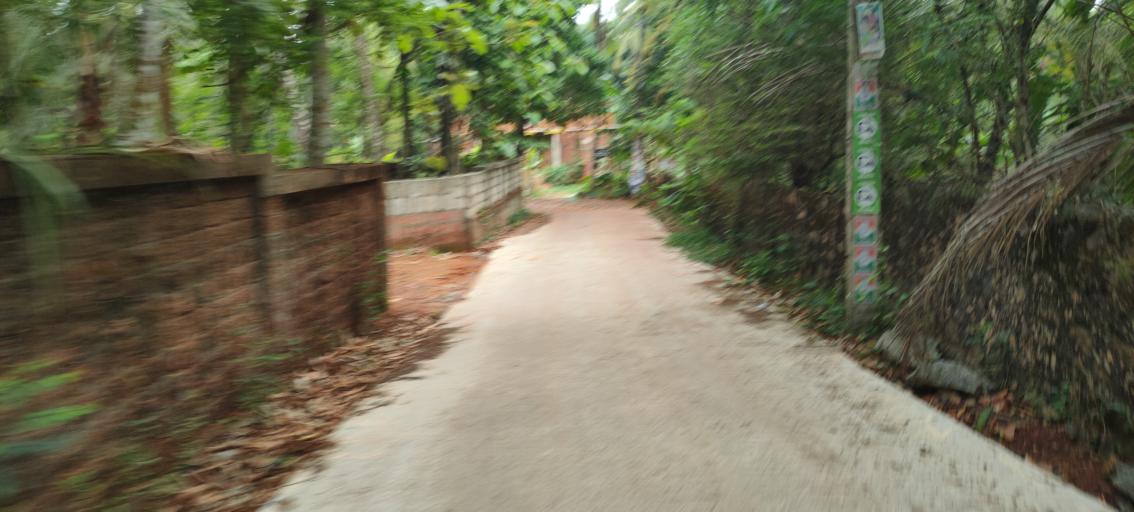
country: IN
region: Kerala
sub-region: Malappuram
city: Ponnani
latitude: 10.7692
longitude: 76.0318
